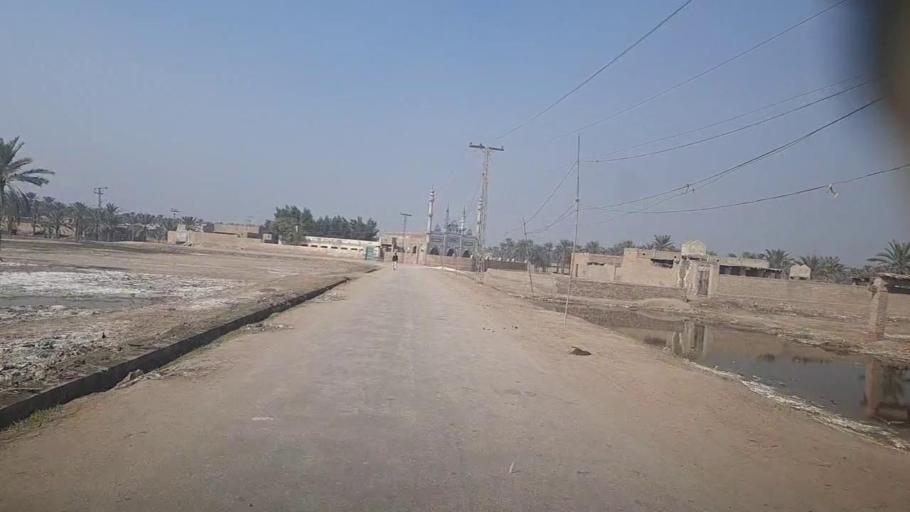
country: PK
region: Sindh
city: Khairpur
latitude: 27.5520
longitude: 68.7827
